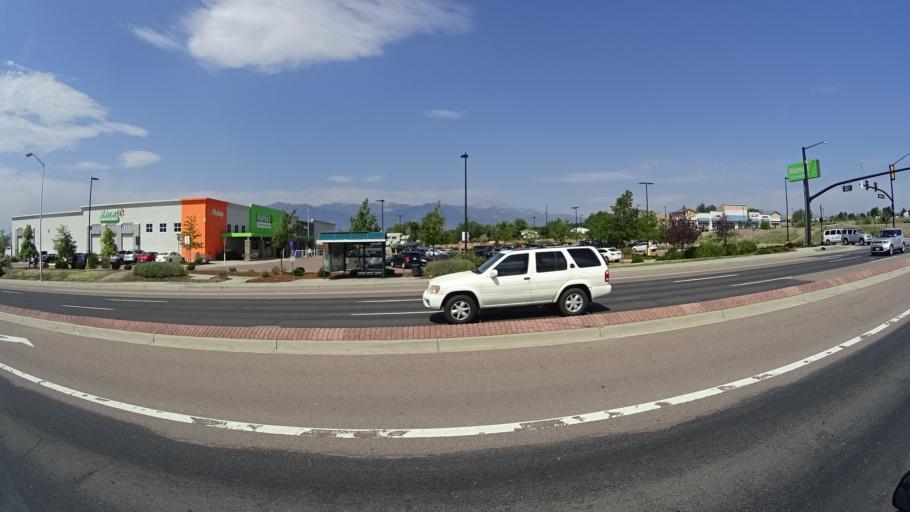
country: US
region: Colorado
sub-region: El Paso County
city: Stratmoor
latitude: 38.8080
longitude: -104.7574
